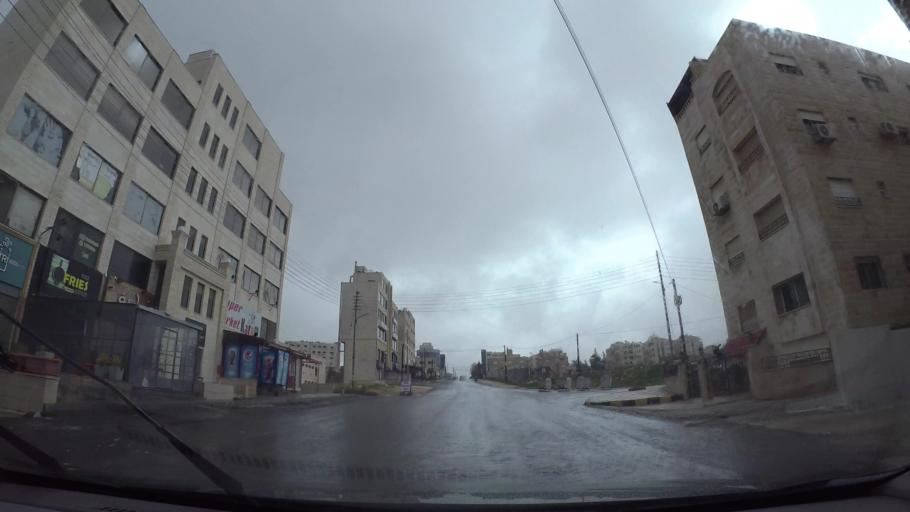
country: JO
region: Amman
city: Wadi as Sir
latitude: 31.9741
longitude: 35.8465
